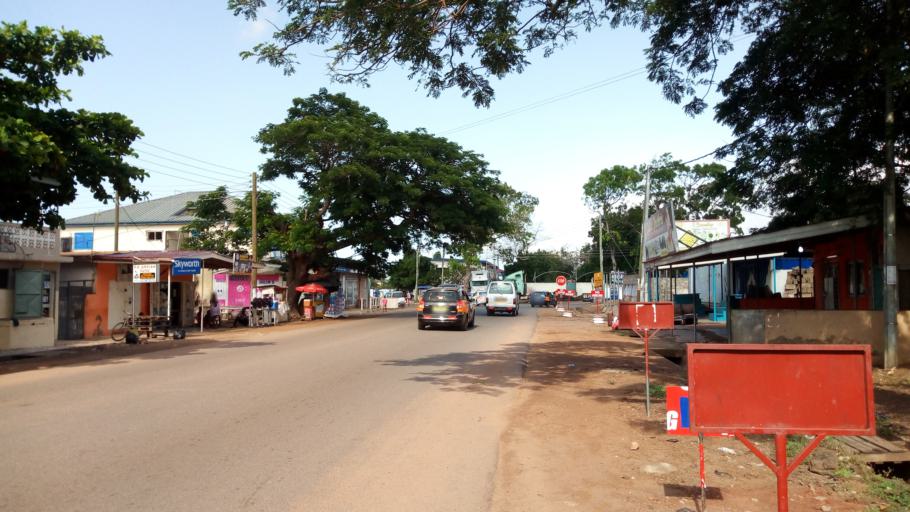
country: GH
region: Greater Accra
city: Tema
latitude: 5.6426
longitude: -0.0037
